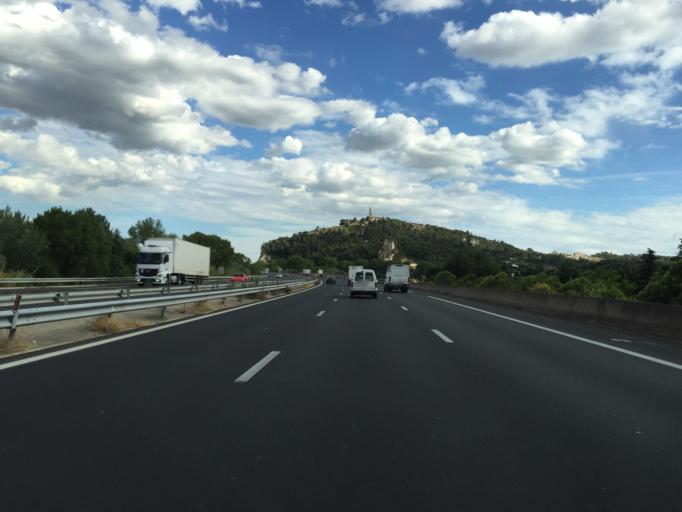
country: FR
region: Provence-Alpes-Cote d'Azur
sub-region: Departement des Bouches-du-Rhone
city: Orgon
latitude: 43.7967
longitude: 5.0401
